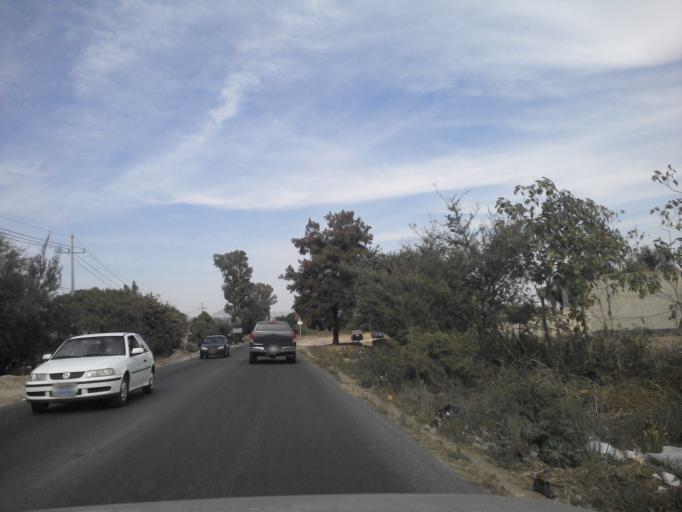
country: MX
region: Jalisco
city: San Sebastian el Grande
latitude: 20.5115
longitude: -103.4125
